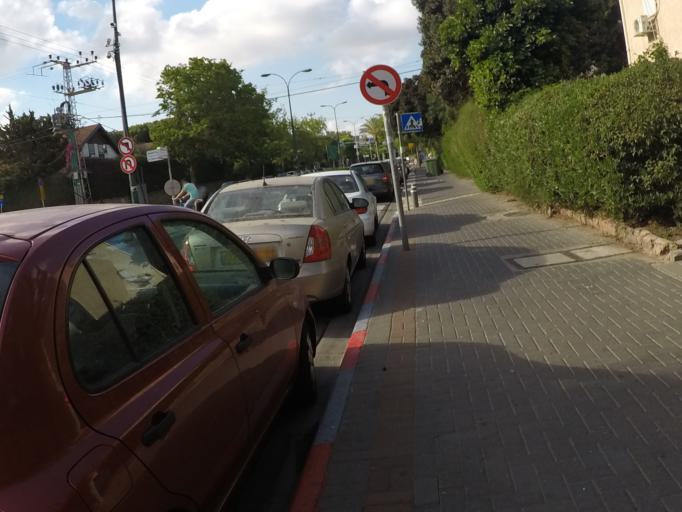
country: IL
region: Tel Aviv
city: Ramat Gan
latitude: 32.1112
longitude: 34.7980
